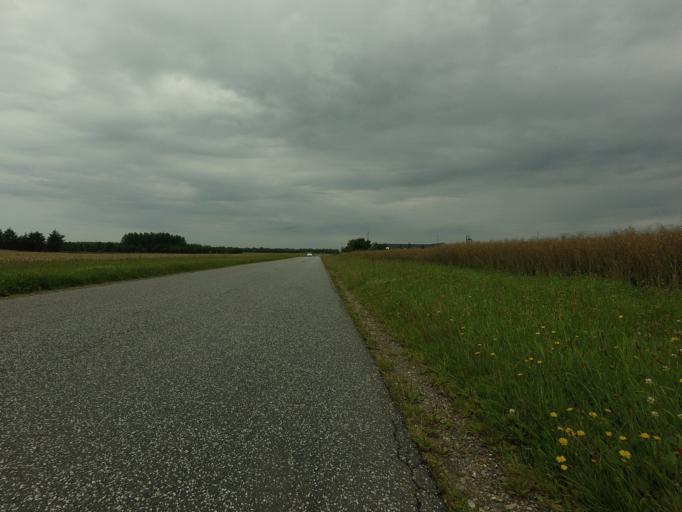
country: DK
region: North Denmark
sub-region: Alborg Kommune
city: Vadum
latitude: 57.1282
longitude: 9.8542
